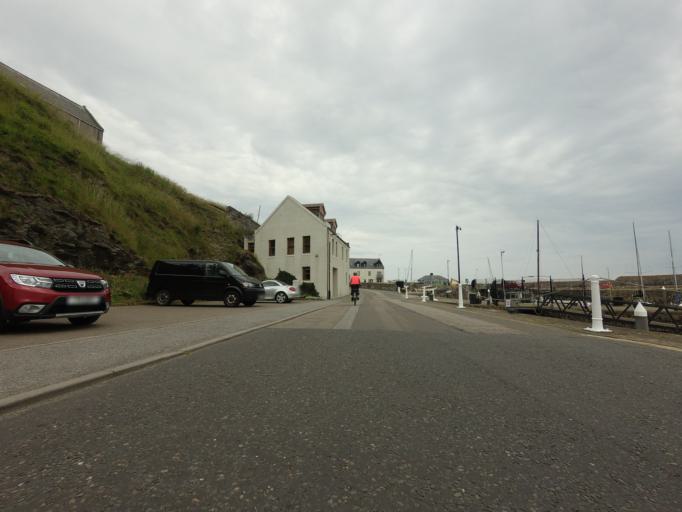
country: GB
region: Scotland
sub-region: Aberdeenshire
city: Banff
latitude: 57.6697
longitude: -2.5234
